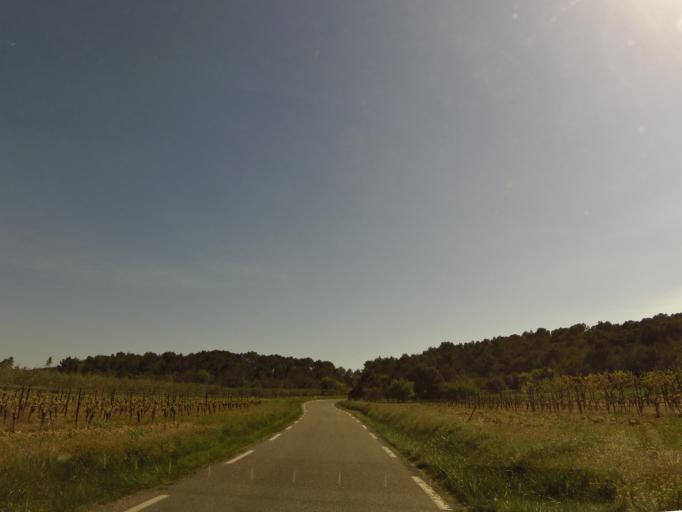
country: FR
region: Languedoc-Roussillon
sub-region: Departement du Gard
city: Congenies
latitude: 43.7681
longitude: 4.1592
